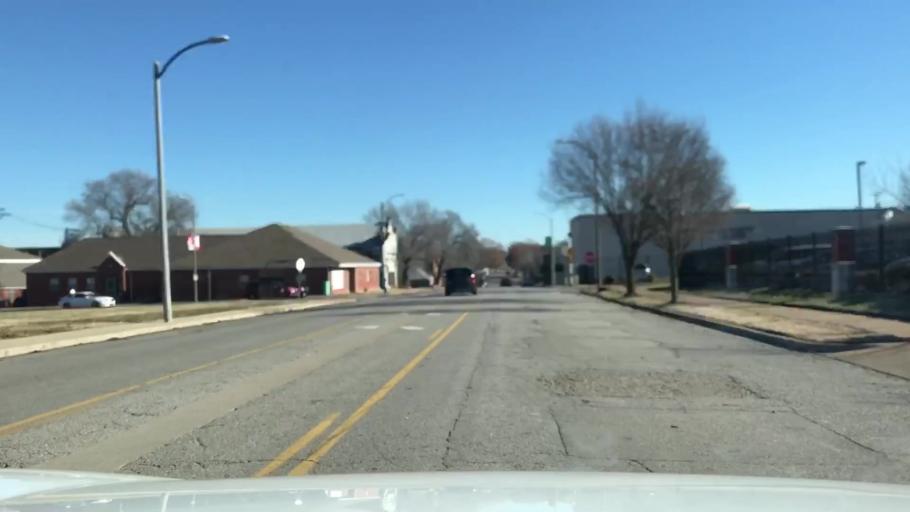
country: US
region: Missouri
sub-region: City of Saint Louis
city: St. Louis
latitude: 38.6198
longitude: -90.2324
